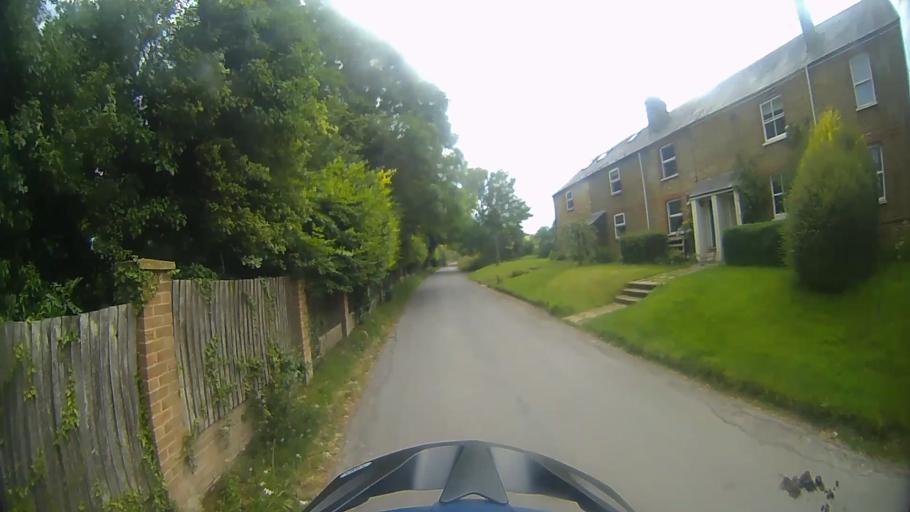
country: GB
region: England
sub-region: Oxfordshire
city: Wantage
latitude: 51.5713
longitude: -1.4494
